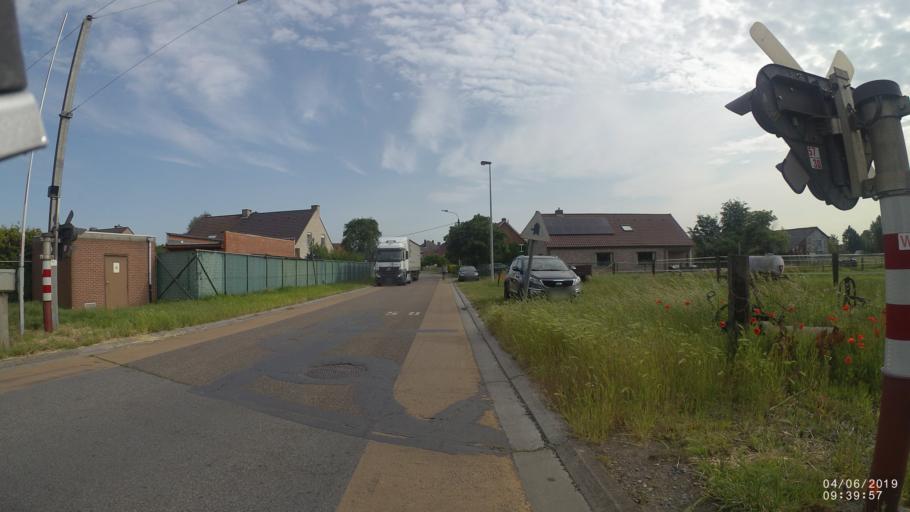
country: BE
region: Flanders
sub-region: Provincie Oost-Vlaanderen
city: Lokeren
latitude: 51.0884
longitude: 4.0070
